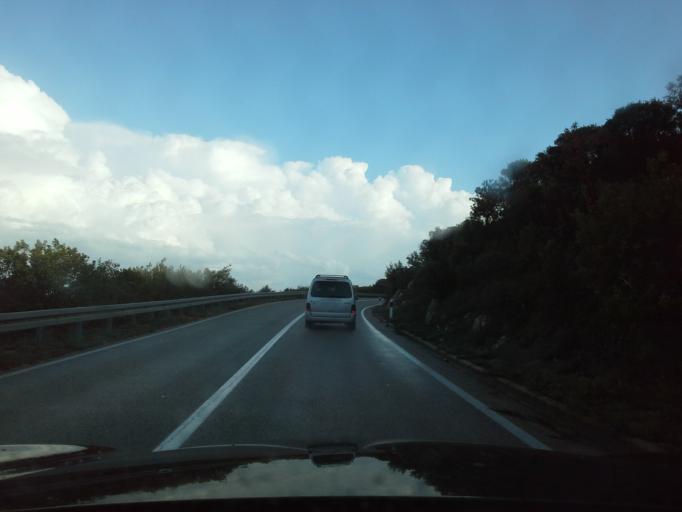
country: HR
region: Primorsko-Goranska
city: Mali Losinj
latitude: 44.6091
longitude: 14.4019
